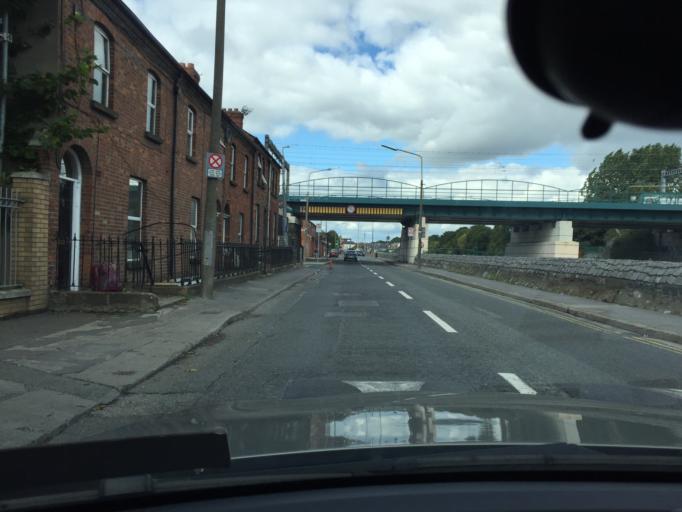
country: IE
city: Fairview
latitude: 53.3582
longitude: -6.2349
